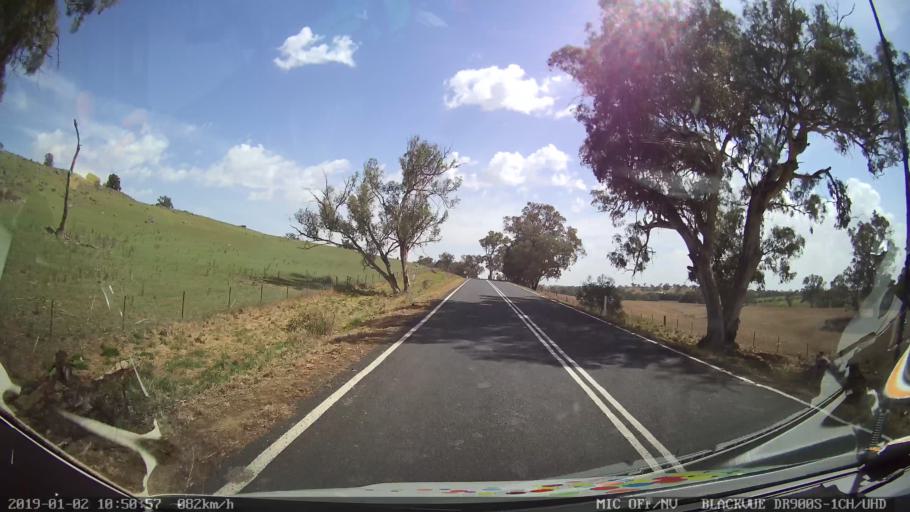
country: AU
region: New South Wales
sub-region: Cootamundra
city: Cootamundra
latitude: -34.7066
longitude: 148.2755
